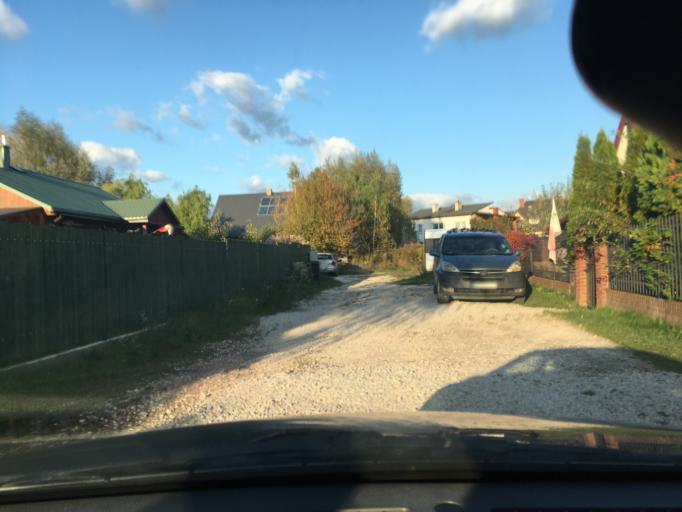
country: PL
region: Masovian Voivodeship
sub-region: Powiat piaseczynski
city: Lesznowola
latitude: 52.0483
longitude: 20.9308
